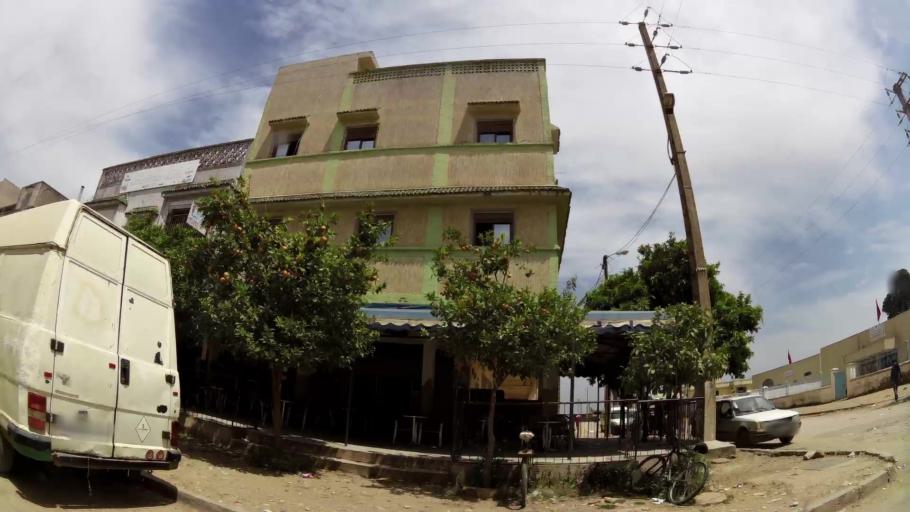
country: MA
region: Rabat-Sale-Zemmour-Zaer
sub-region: Khemisset
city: Khemisset
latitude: 33.8147
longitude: -6.0683
